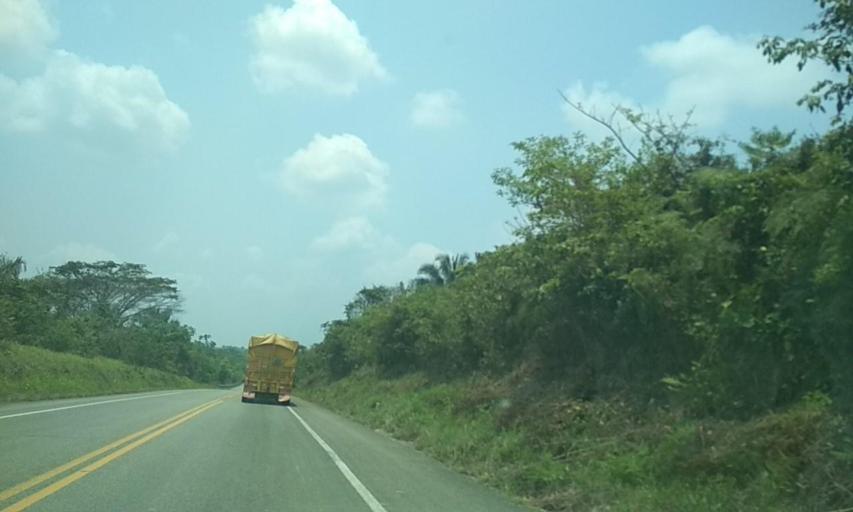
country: MX
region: Tabasco
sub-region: Huimanguillo
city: Francisco Rueda
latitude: 17.7328
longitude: -93.9707
